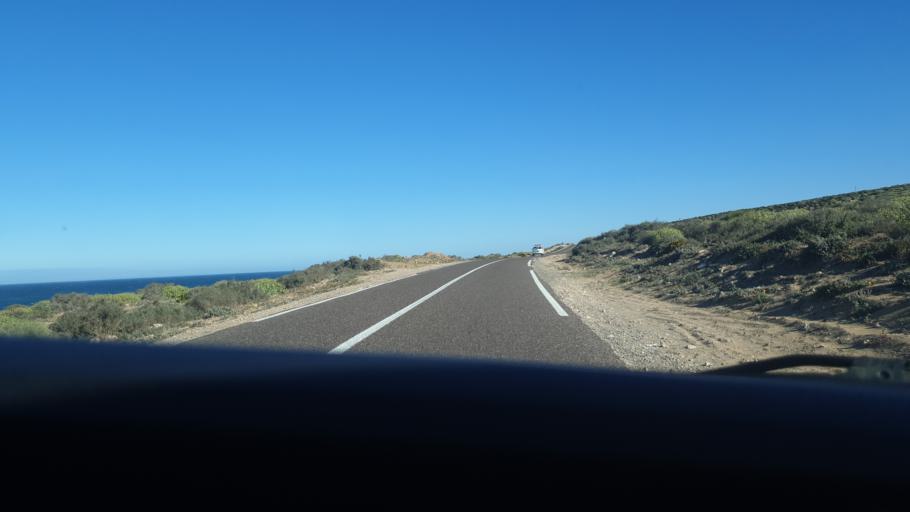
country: MA
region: Souss-Massa-Draa
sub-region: Agadir-Ida-ou-Tnan
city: Tamri
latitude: 30.6668
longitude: -9.8836
